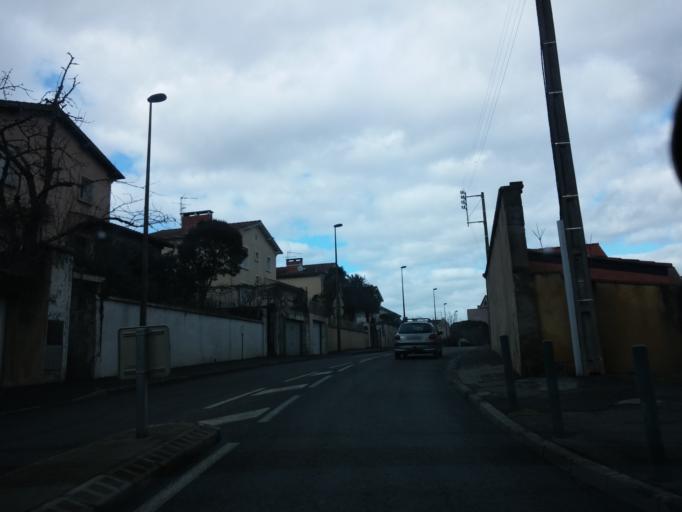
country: FR
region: Midi-Pyrenees
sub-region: Departement de la Haute-Garonne
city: Blagnac
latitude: 43.6149
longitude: 1.3997
